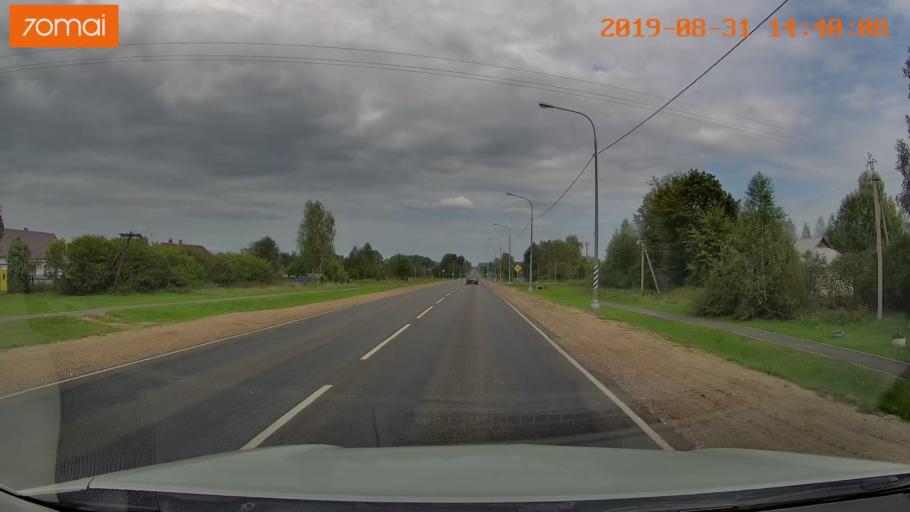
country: RU
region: Smolensk
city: Yekimovichi
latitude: 54.1956
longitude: 33.5663
